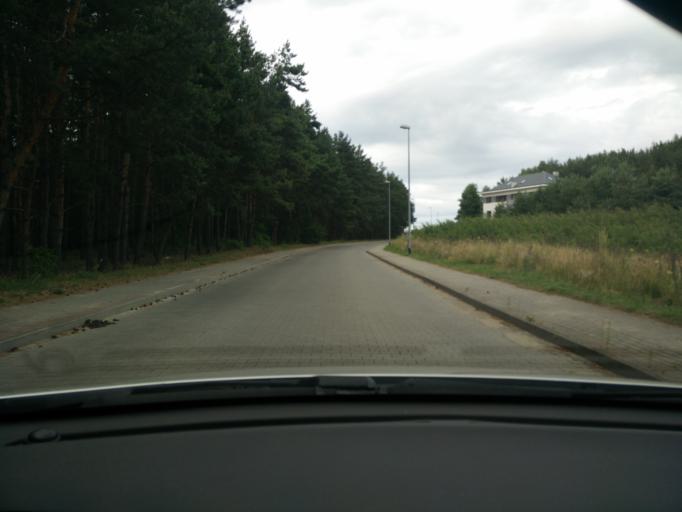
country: PL
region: Pomeranian Voivodeship
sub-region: Powiat pucki
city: Kosakowo
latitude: 54.6028
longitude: 18.4852
